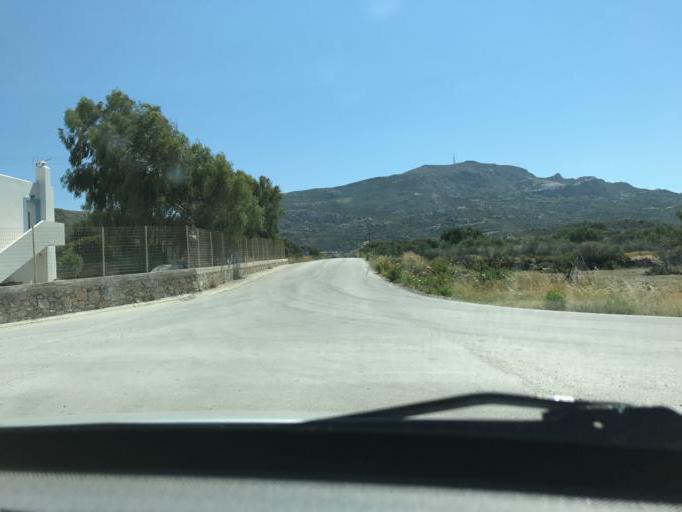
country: GR
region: South Aegean
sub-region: Nomos Dodekanisou
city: Karpathos
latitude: 35.4985
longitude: 27.1914
